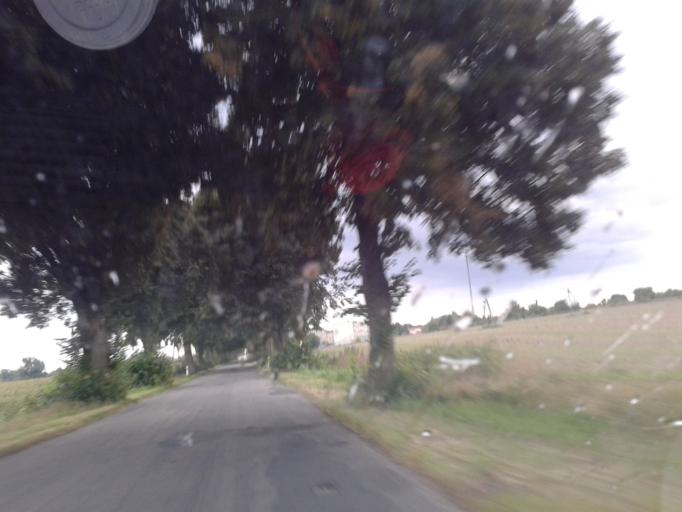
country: PL
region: West Pomeranian Voivodeship
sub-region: Powiat szczecinecki
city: Grzmiaca
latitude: 53.8419
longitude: 16.4440
